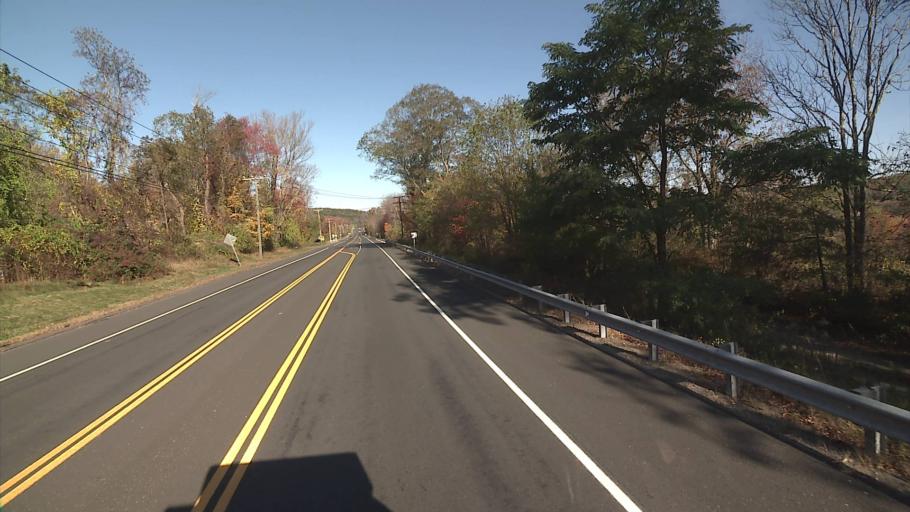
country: US
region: Connecticut
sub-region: Tolland County
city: Coventry Lake
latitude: 41.7504
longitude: -72.3960
